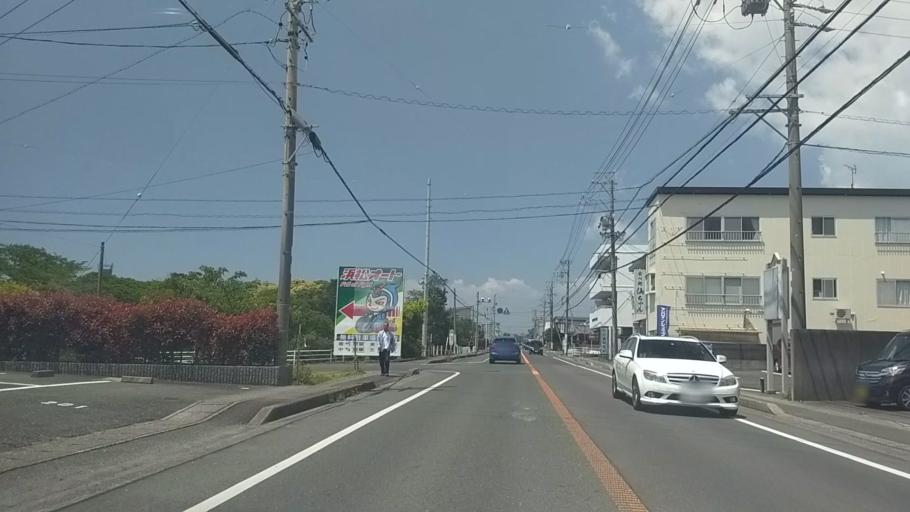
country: JP
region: Shizuoka
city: Hamamatsu
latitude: 34.7391
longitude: 137.7071
